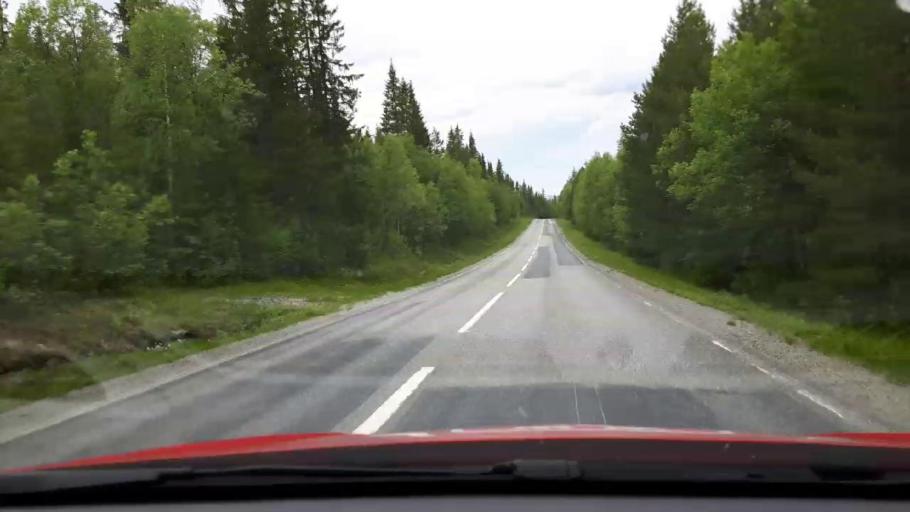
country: NO
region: Hedmark
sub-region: Engerdal
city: Engerdal
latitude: 62.4256
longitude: 12.7295
